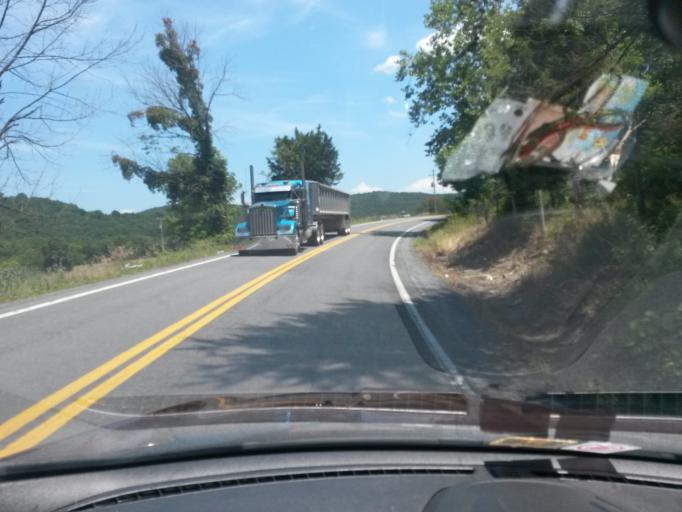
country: US
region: West Virginia
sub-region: Grant County
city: Petersburg
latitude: 39.1164
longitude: -79.1565
